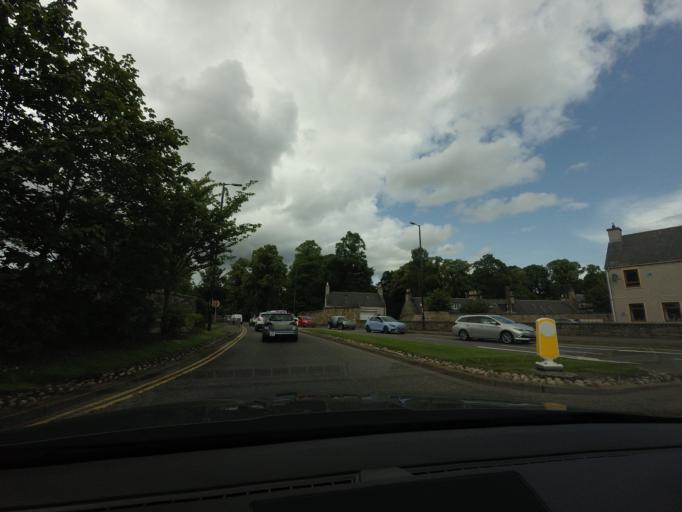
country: GB
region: Scotland
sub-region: Moray
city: Elgin
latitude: 57.6489
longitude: -3.3082
